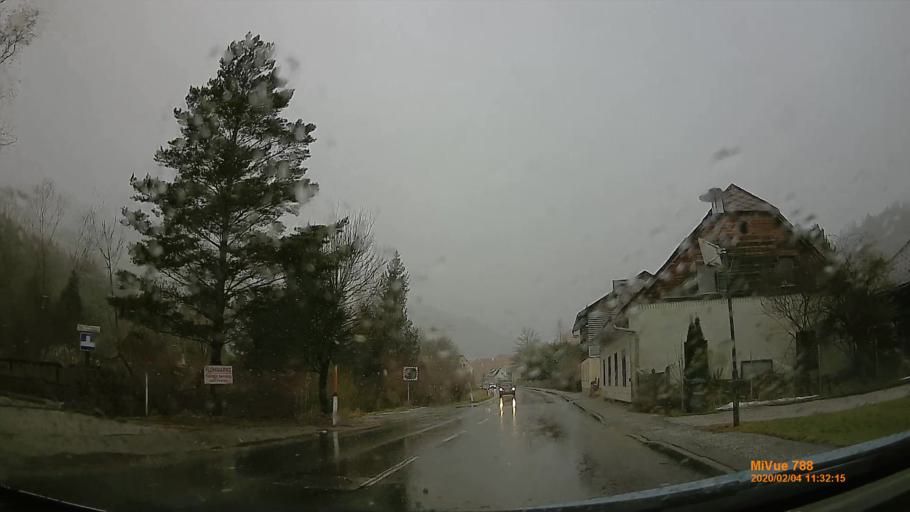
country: AT
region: Styria
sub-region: Politischer Bezirk Bruck-Muerzzuschlag
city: Neuberg an der Muerz
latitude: 47.6598
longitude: 15.5829
